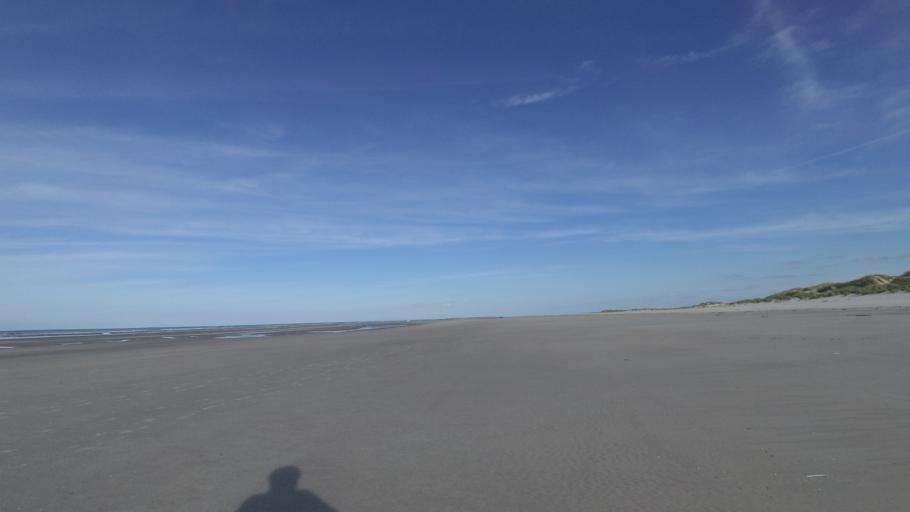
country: NL
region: Friesland
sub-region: Gemeente Dongeradeel
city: Ternaard
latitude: 53.4679
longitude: 5.9189
